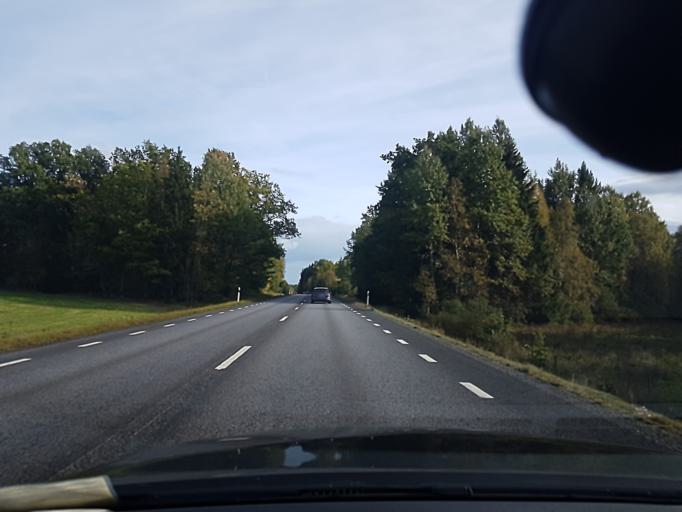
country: SE
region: Joenkoeping
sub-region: Varnamo Kommun
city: Bor
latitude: 57.1426
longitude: 14.1033
